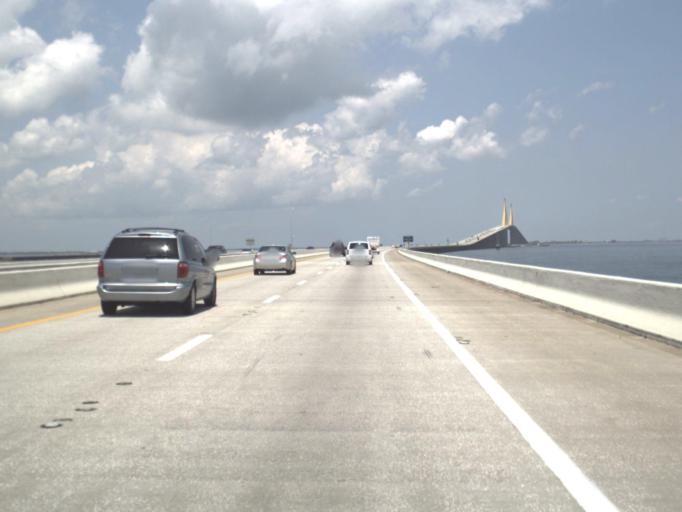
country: US
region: Florida
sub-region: Manatee County
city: West Bradenton
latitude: 27.5991
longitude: -82.6384
